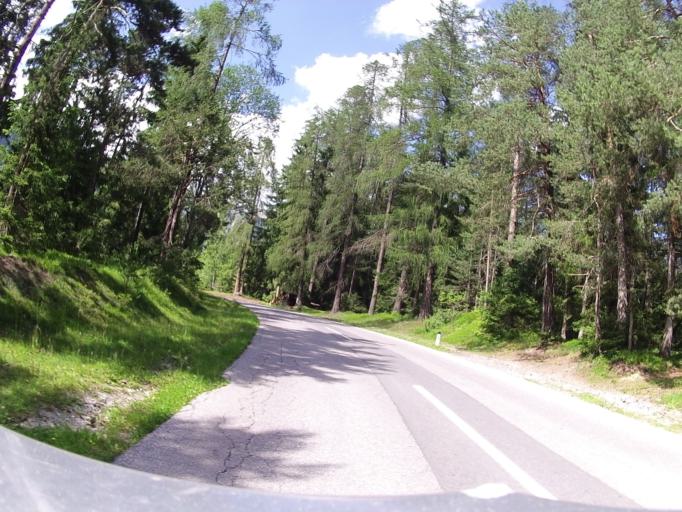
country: AT
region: Tyrol
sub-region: Politischer Bezirk Imst
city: Imst
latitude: 47.2579
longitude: 10.7384
